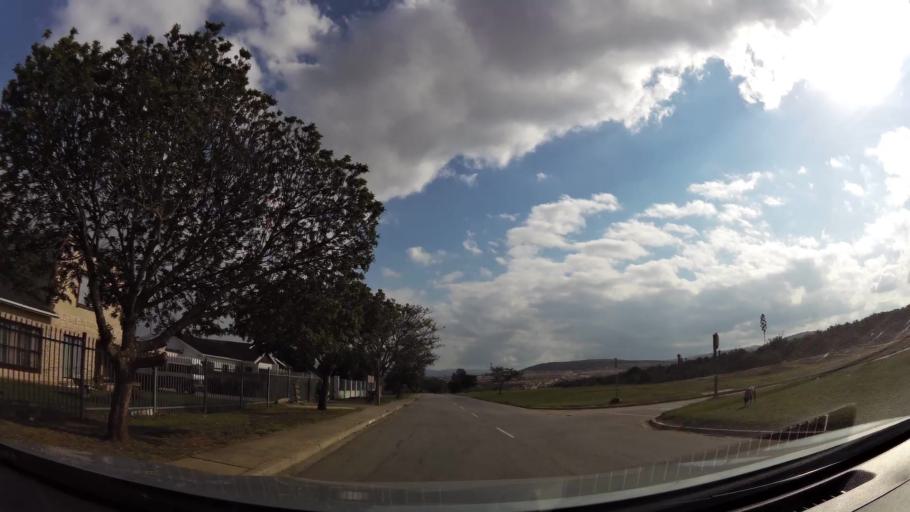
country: ZA
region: Eastern Cape
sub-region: Nelson Mandela Bay Metropolitan Municipality
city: Uitenhage
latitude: -33.7309
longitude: 25.4097
